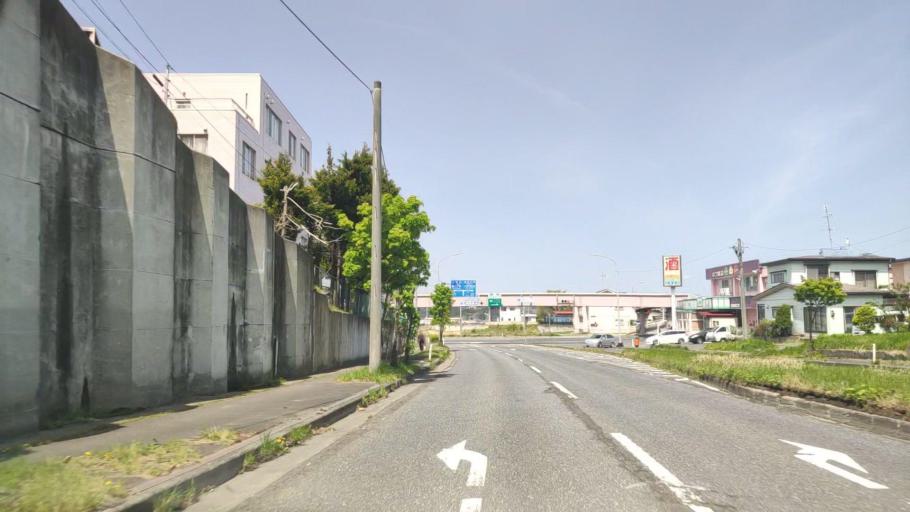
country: JP
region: Aomori
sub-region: Hachinohe Shi
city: Uchimaru
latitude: 40.5011
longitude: 141.4552
